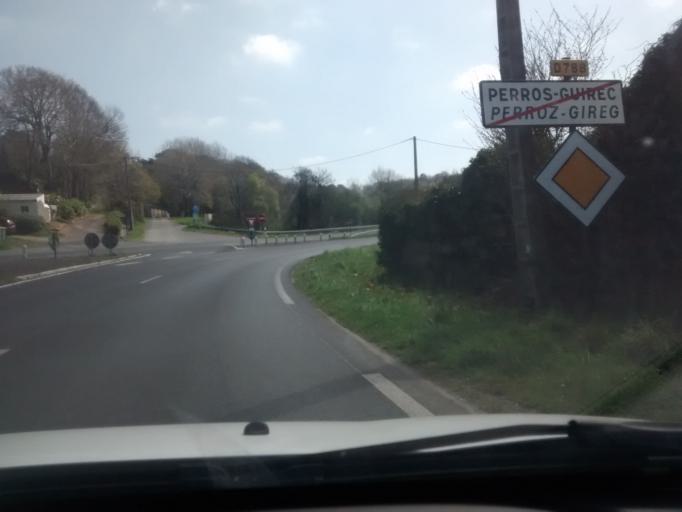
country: FR
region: Brittany
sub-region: Departement des Cotes-d'Armor
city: Saint-Quay-Perros
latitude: 48.7970
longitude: -3.4413
